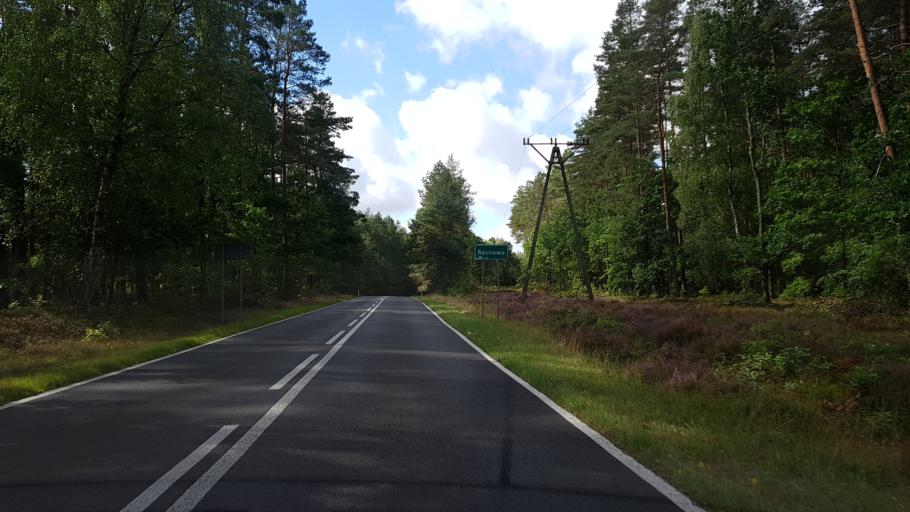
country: PL
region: West Pomeranian Voivodeship
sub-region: Powiat koszalinski
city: Sianow
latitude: 54.0772
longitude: 16.2992
